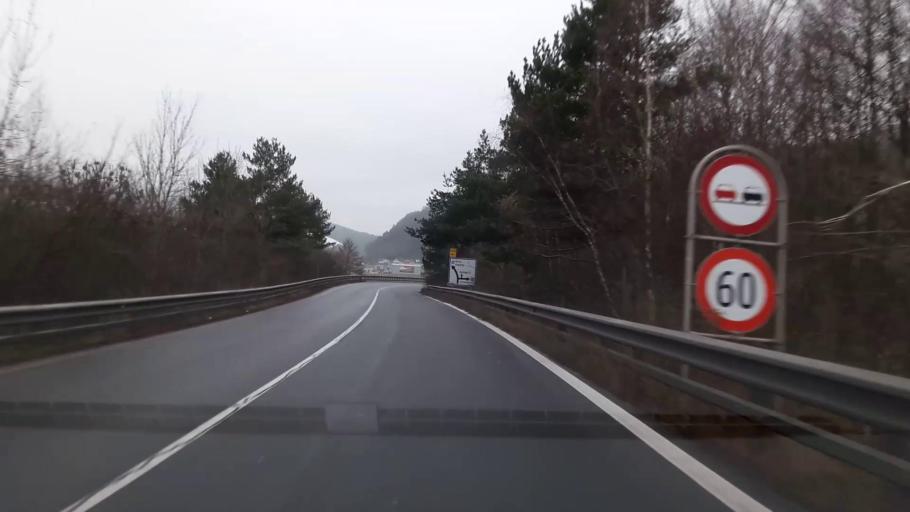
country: AT
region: Lower Austria
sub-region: Politischer Bezirk Neunkirchen
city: Grimmenstein
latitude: 47.6083
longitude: 16.1238
